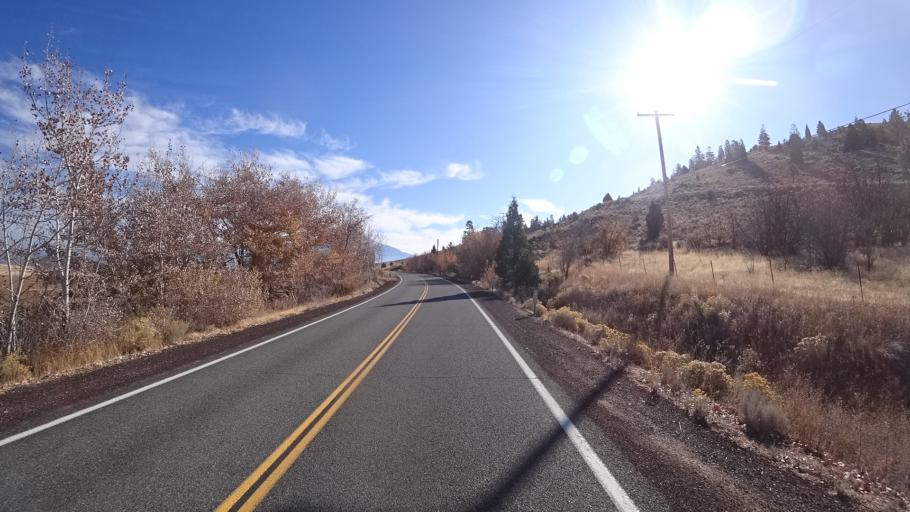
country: US
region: California
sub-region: Siskiyou County
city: Weed
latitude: 41.4690
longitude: -122.4729
